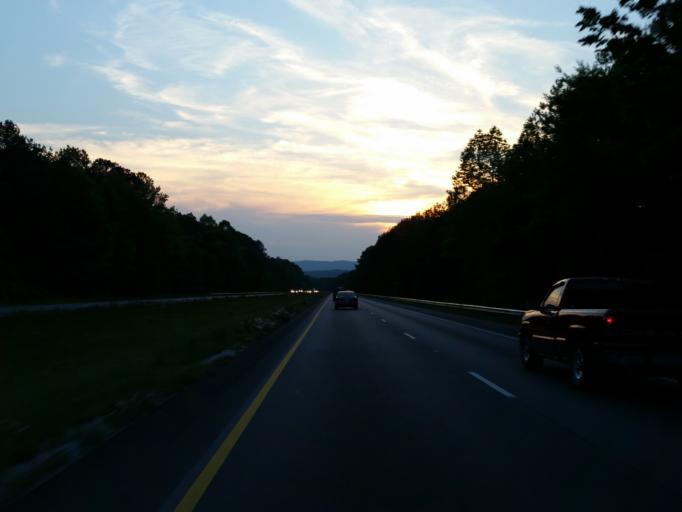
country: US
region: Alabama
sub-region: Calhoun County
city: Choccolocco
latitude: 33.6164
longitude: -85.6926
